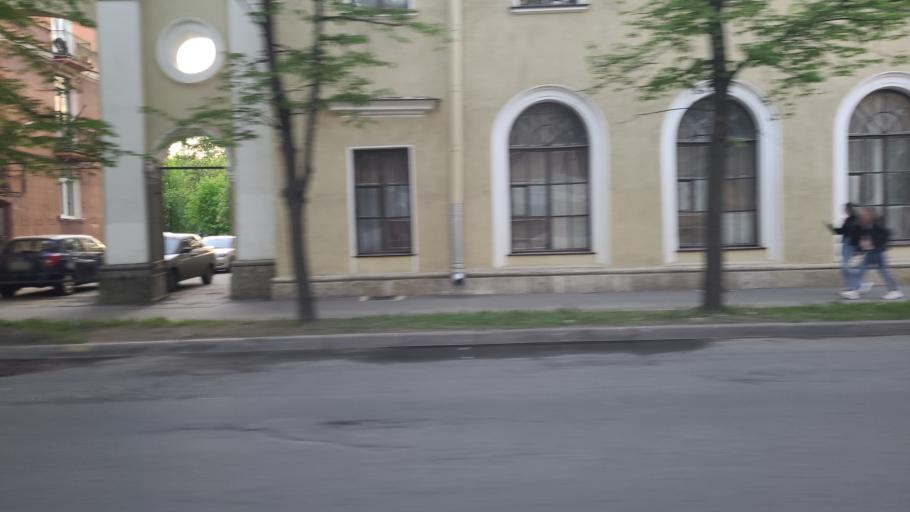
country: RU
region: St.-Petersburg
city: Kolpino
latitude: 59.7482
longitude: 30.6109
